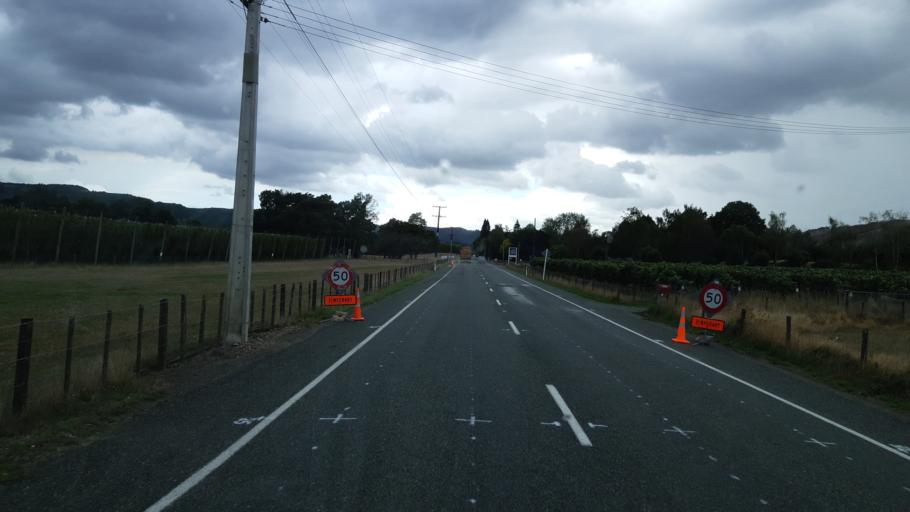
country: NZ
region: Tasman
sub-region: Tasman District
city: Wakefield
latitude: -41.4191
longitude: 173.0078
